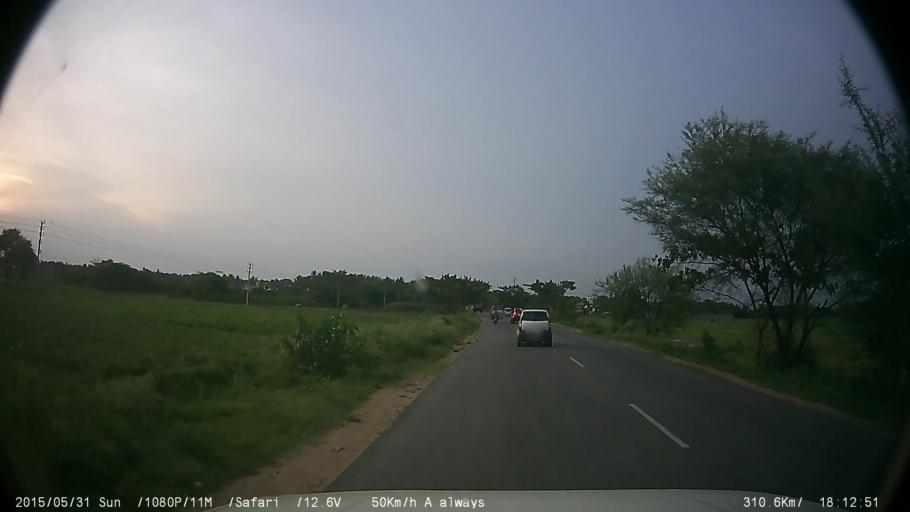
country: IN
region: Karnataka
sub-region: Mysore
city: Nanjangud
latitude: 12.0985
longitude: 76.6720
